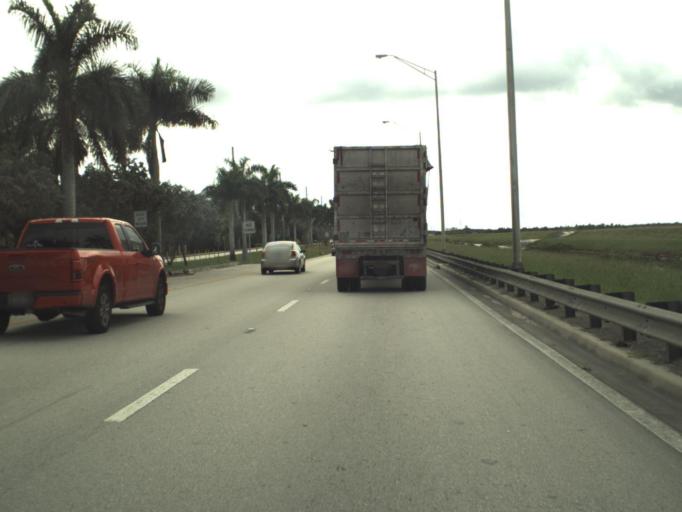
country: US
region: Florida
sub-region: Miami-Dade County
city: Tamiami
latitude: 25.7611
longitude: -80.4359
